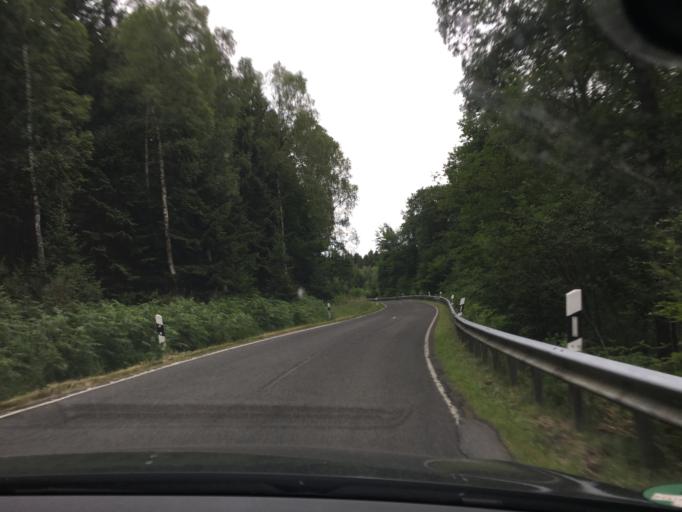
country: DE
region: North Rhine-Westphalia
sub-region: Regierungsbezirk Koln
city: Langerwehe
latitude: 50.7673
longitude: 6.3532
